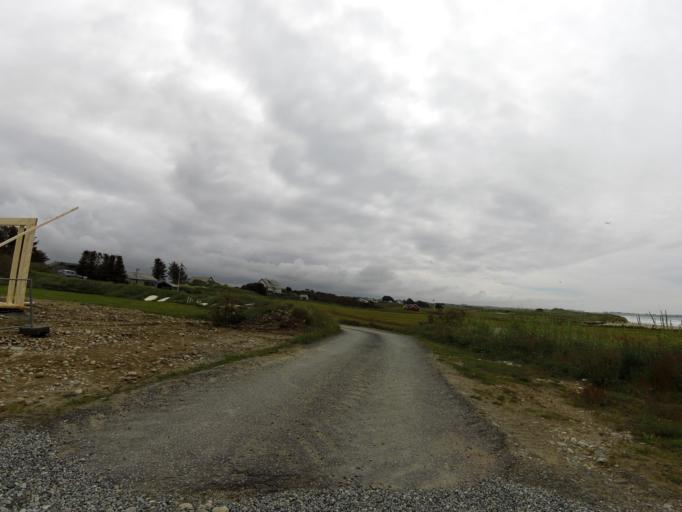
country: NO
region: Rogaland
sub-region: Klepp
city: Kleppe
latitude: 58.8136
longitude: 5.5494
